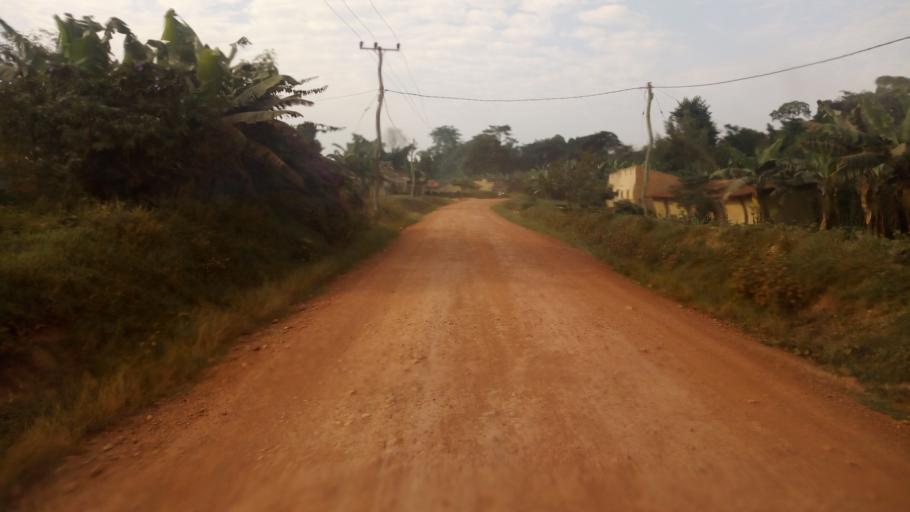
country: UG
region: Western Region
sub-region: Kanungu District
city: Ntungamo
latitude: -0.8431
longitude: 29.6417
